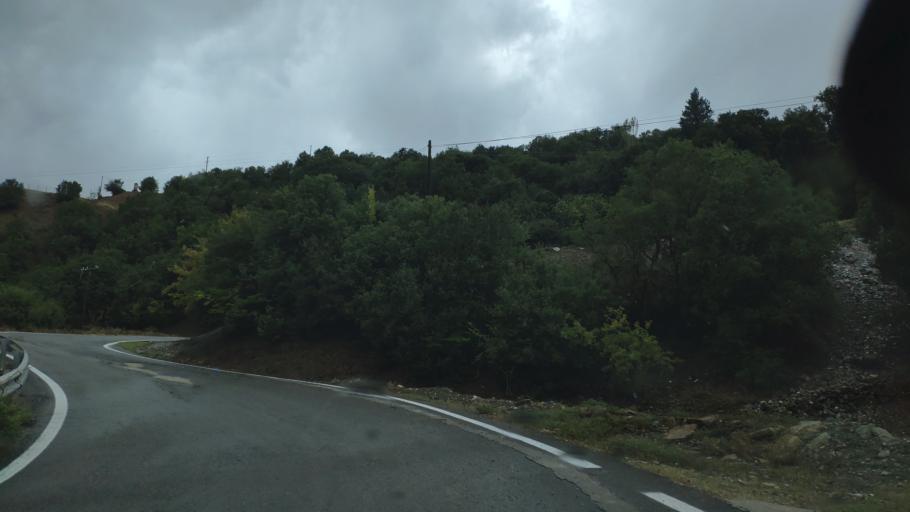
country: GR
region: Thessaly
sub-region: Nomos Kardhitsas
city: Anthiro
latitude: 39.1077
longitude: 21.4121
